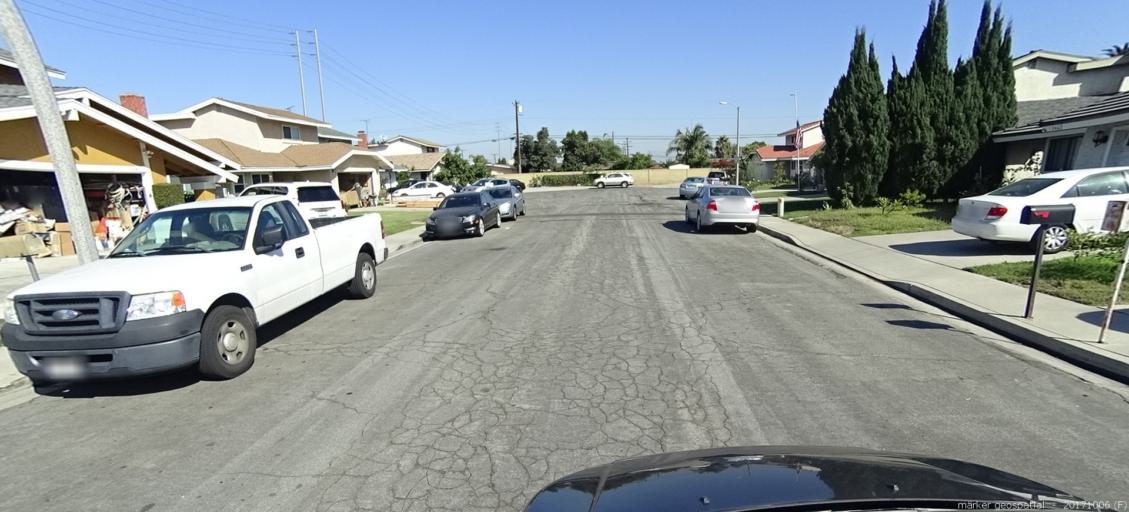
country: US
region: California
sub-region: Orange County
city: Stanton
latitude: 33.7814
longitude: -117.9790
